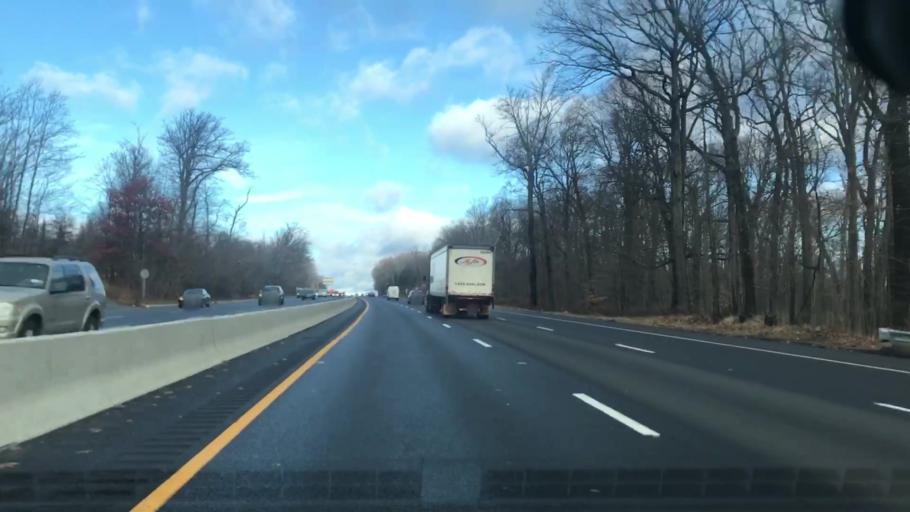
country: US
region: New Jersey
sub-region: Bergen County
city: Saddle River
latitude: 41.0370
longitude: -74.1125
